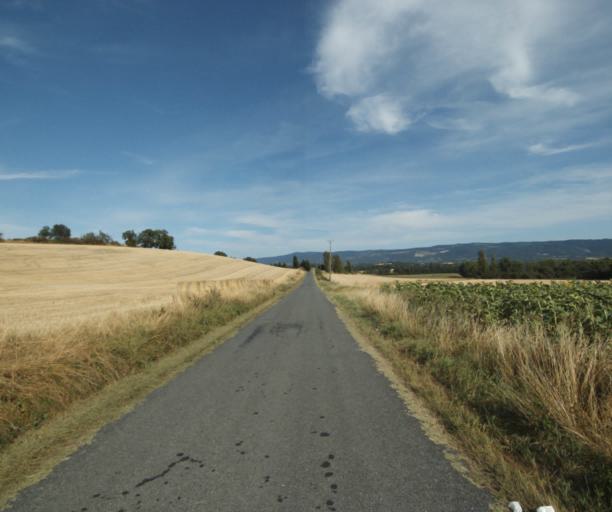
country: FR
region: Midi-Pyrenees
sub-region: Departement du Tarn
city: Puylaurens
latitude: 43.5258
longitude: 2.0513
